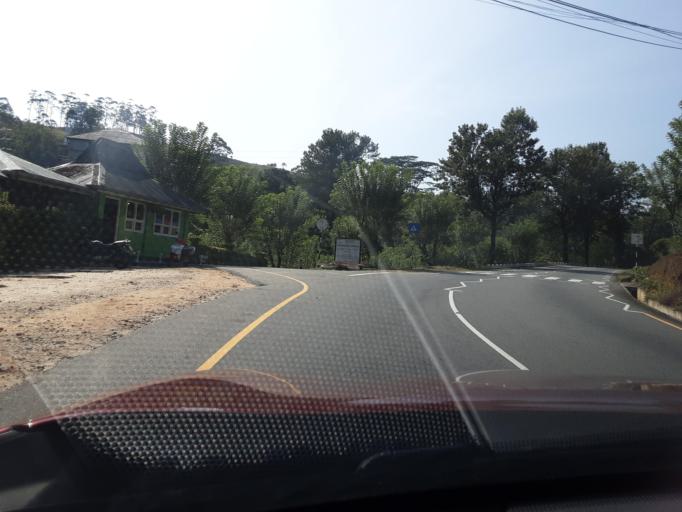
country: LK
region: Uva
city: Badulla
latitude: 6.9574
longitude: 81.1194
